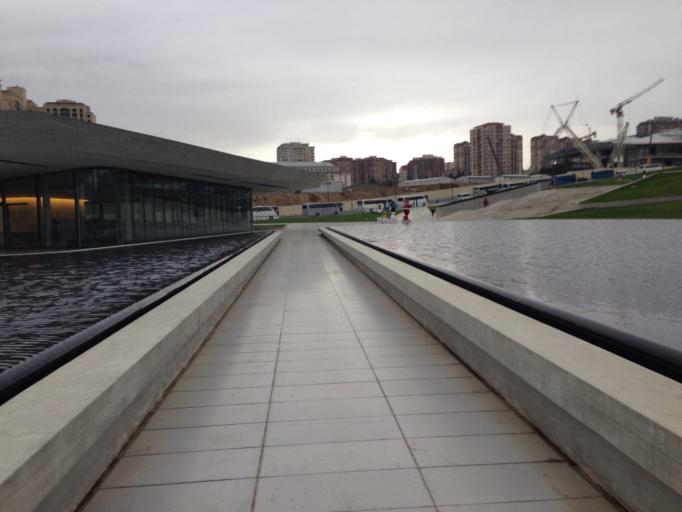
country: AZ
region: Baki
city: Baku
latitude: 40.3930
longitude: 49.8661
